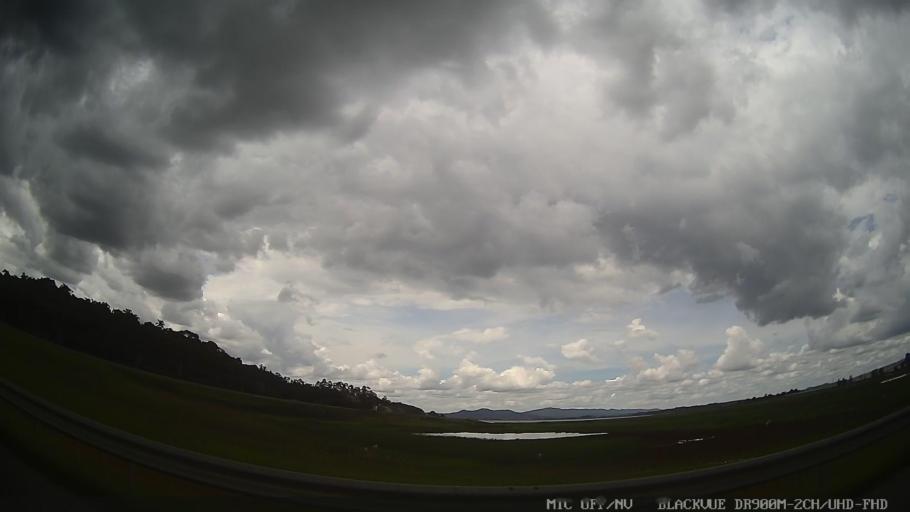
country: BR
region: Sao Paulo
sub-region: Suzano
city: Suzano
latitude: -23.6104
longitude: -46.2980
